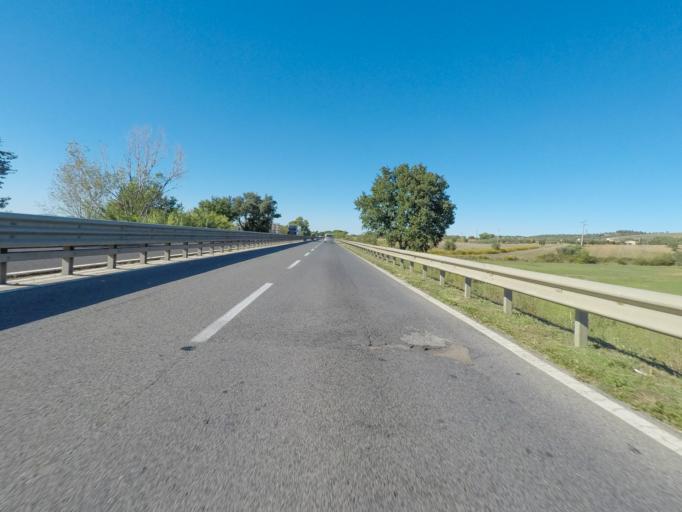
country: IT
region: Tuscany
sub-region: Provincia di Grosseto
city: Grosseto
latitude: 42.7183
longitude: 11.1415
